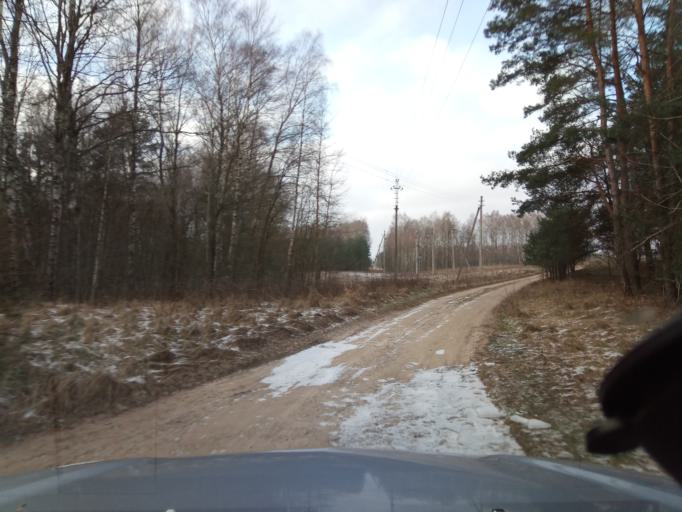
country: LT
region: Alytaus apskritis
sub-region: Alytaus rajonas
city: Daugai
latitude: 54.3772
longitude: 24.4099
